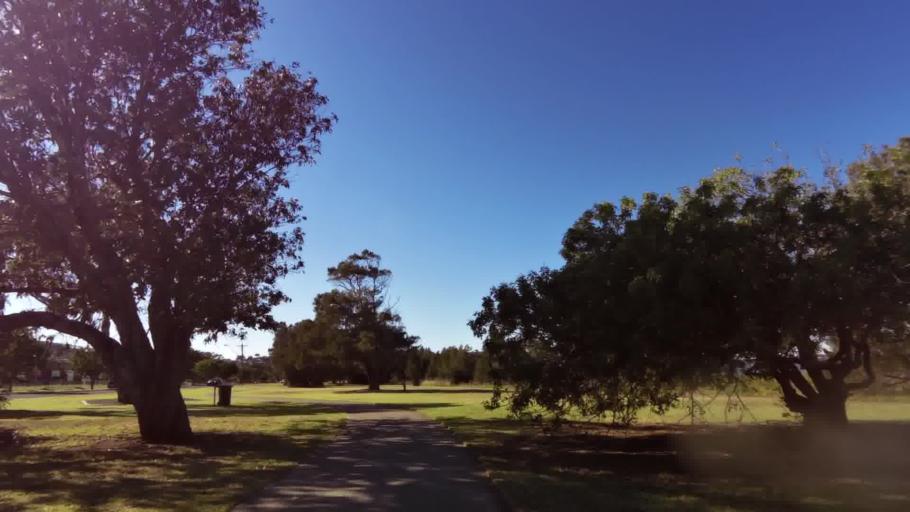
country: AU
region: New South Wales
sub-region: Wollongong
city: Berkeley
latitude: -34.4838
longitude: 150.8474
